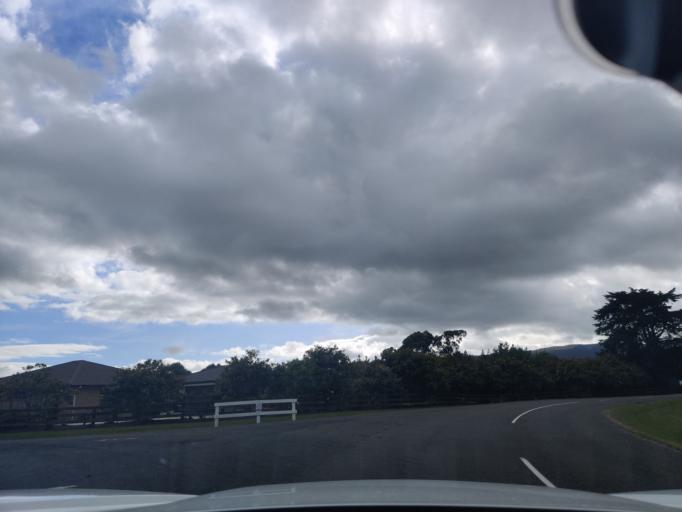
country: NZ
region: Manawatu-Wanganui
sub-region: Palmerston North City
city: Palmerston North
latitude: -40.3765
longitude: 175.6603
